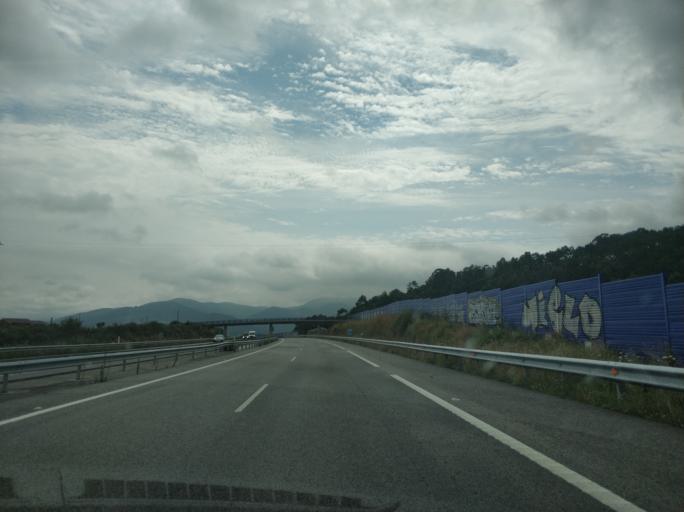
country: ES
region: Asturias
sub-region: Province of Asturias
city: Navia
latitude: 43.5299
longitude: -6.5789
